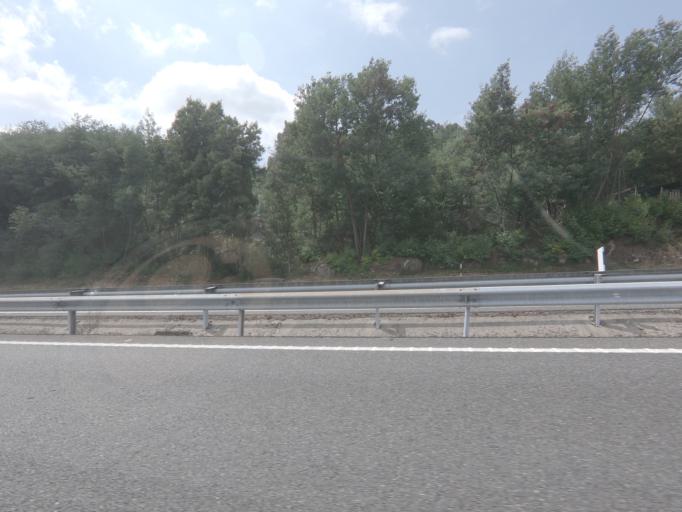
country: ES
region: Galicia
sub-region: Provincia de Pontevedra
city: Tui
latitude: 42.0598
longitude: -8.6504
